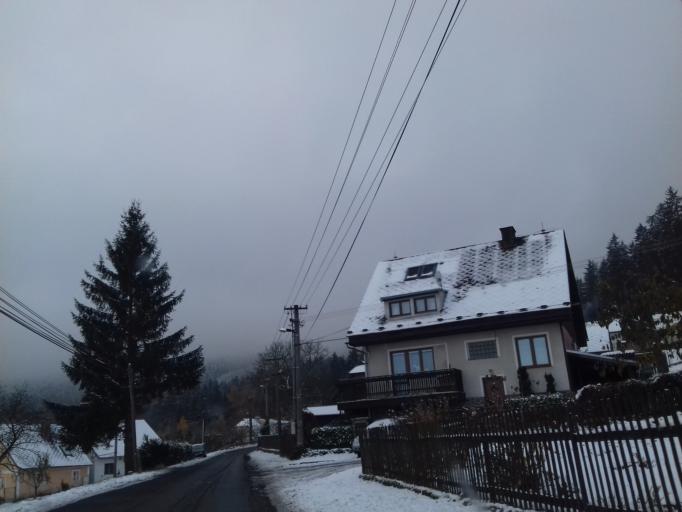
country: CZ
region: Plzensky
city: Postrekov
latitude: 49.4447
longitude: 12.7870
